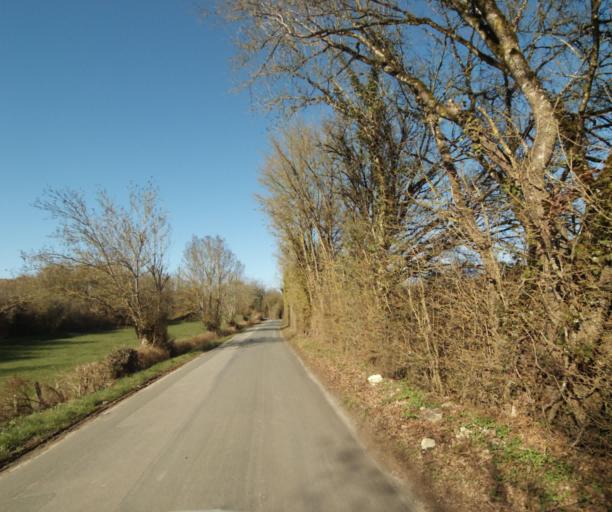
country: FR
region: Poitou-Charentes
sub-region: Departement des Deux-Sevres
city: Bessines
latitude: 46.3365
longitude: -0.5070
